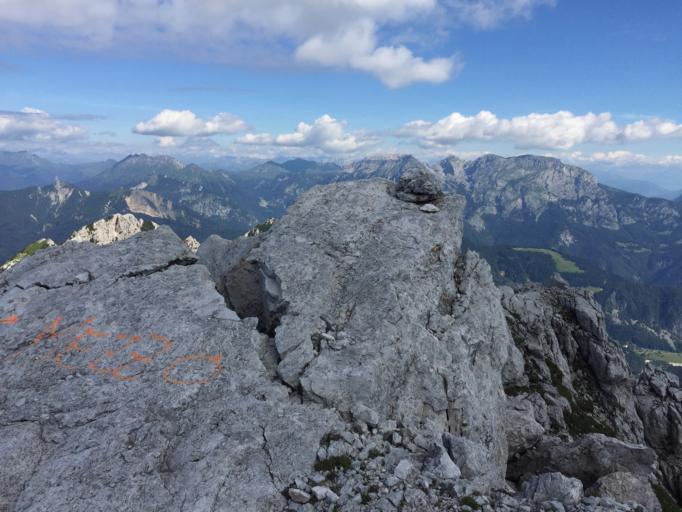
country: IT
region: Friuli Venezia Giulia
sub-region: Provincia di Udine
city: Pontebba
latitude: 46.4700
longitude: 13.2465
